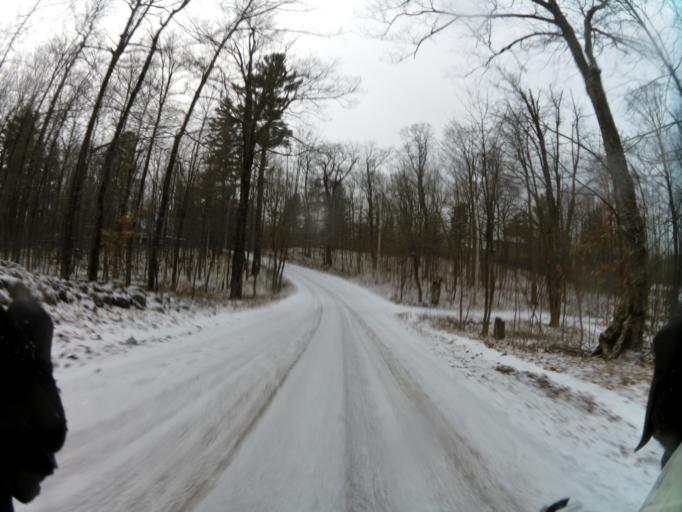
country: CA
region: Quebec
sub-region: Outaouais
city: Gatineau
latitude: 45.4850
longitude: -75.8490
